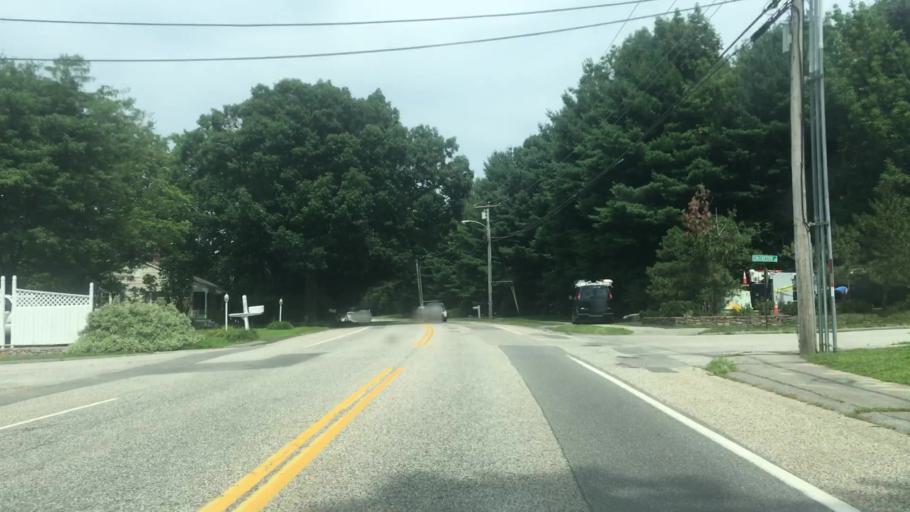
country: US
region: Maine
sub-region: Cumberland County
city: South Portland Gardens
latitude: 43.6092
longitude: -70.2814
